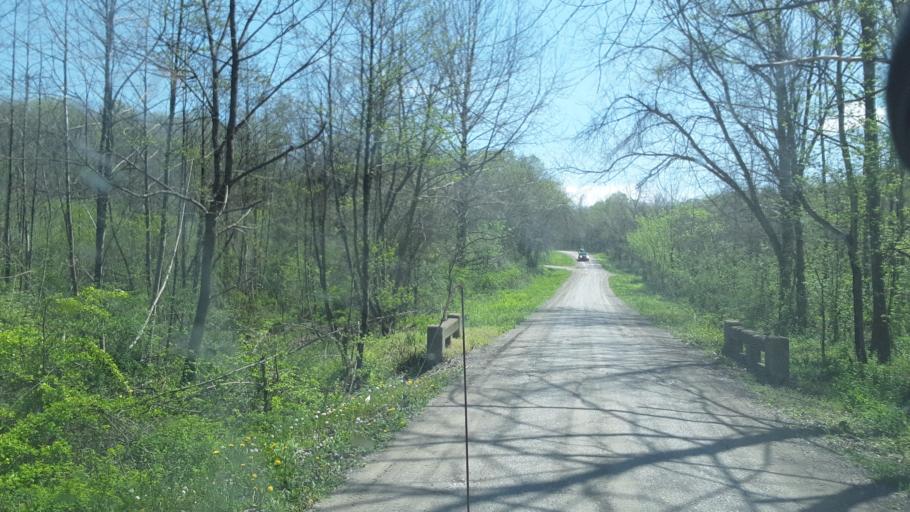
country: US
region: Ohio
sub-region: Noble County
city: Caldwell
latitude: 39.7728
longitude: -81.6342
